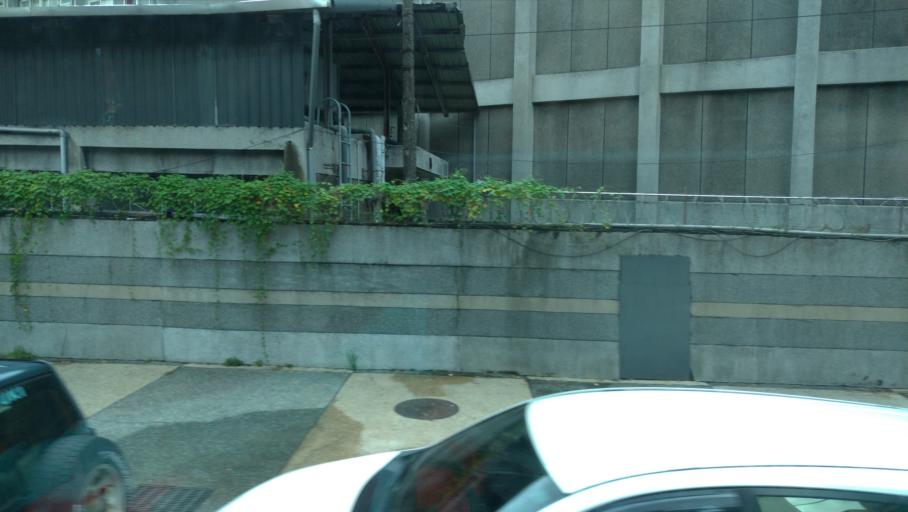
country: TW
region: Taiwan
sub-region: Keelung
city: Keelung
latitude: 25.1363
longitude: 121.7478
